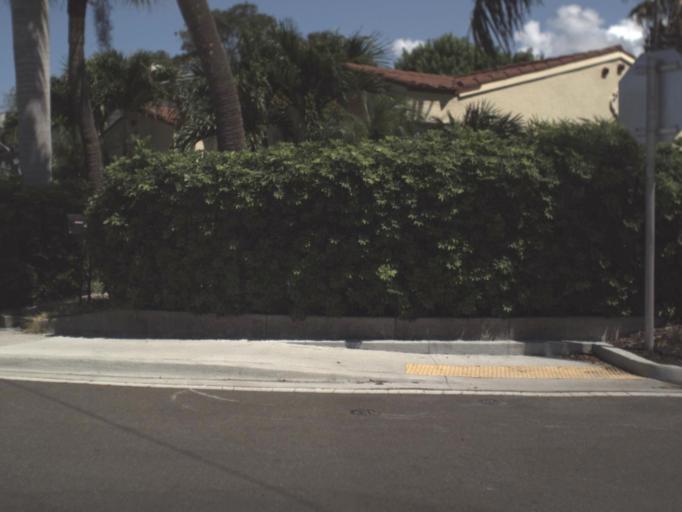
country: US
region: Florida
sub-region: Pinellas County
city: Redington Beach
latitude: 27.8079
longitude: -82.8104
